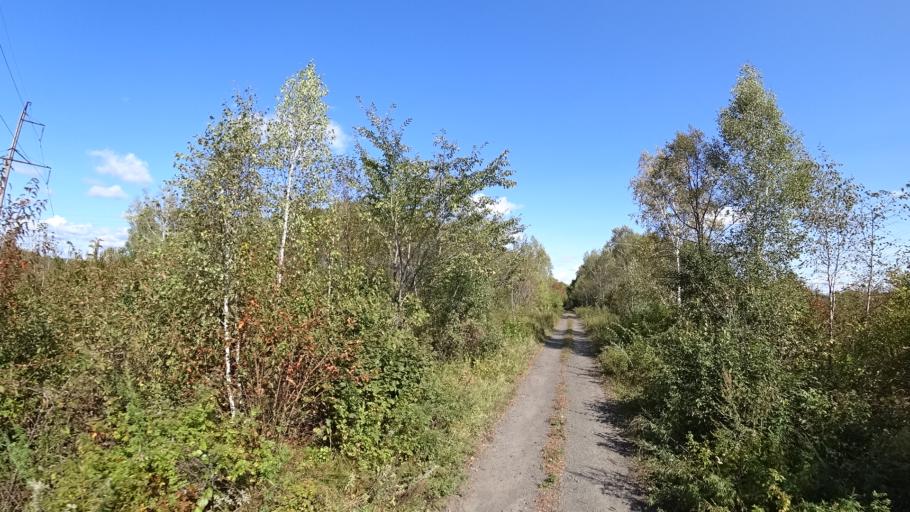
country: RU
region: Amur
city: Arkhara
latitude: 49.4004
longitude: 130.1246
